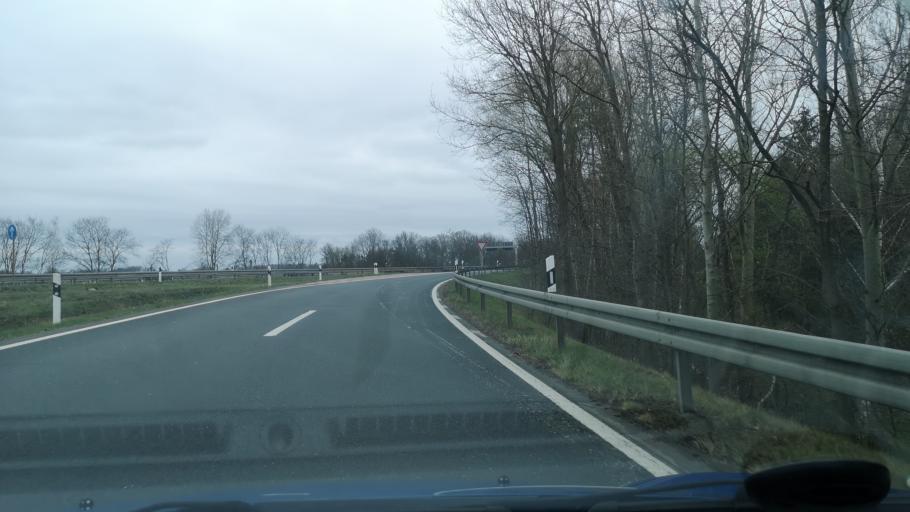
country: DE
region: Lower Saxony
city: Isernhagen Farster Bauerschaft
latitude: 52.4279
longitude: 9.8896
